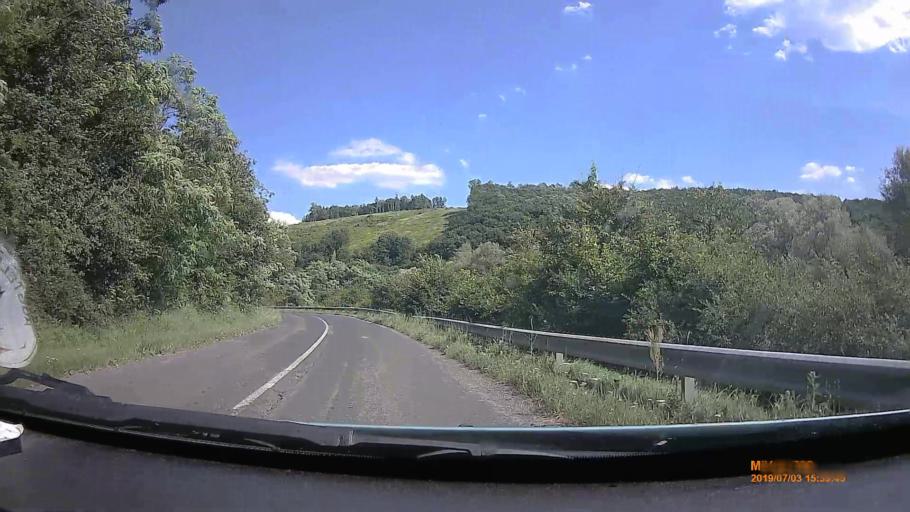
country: HU
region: Heves
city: Szilvasvarad
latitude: 48.1635
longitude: 20.4038
